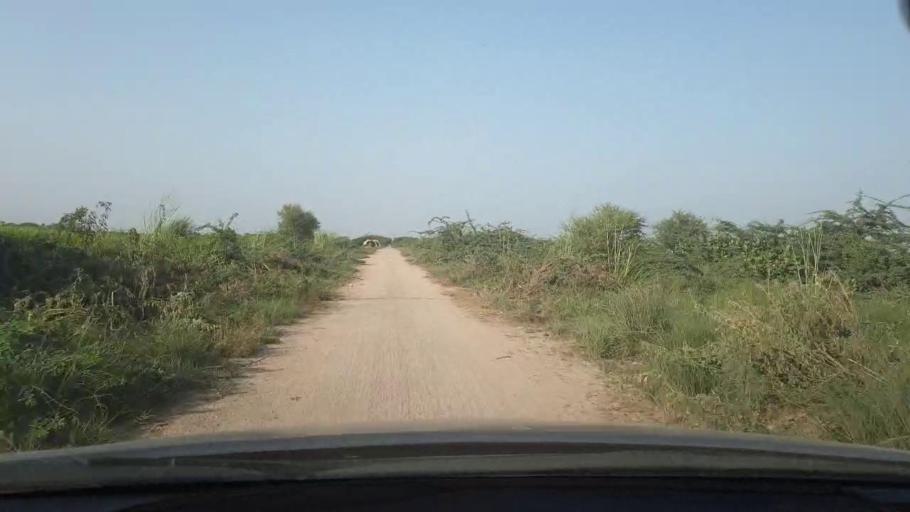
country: PK
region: Sindh
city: Naukot
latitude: 24.7761
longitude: 69.2325
